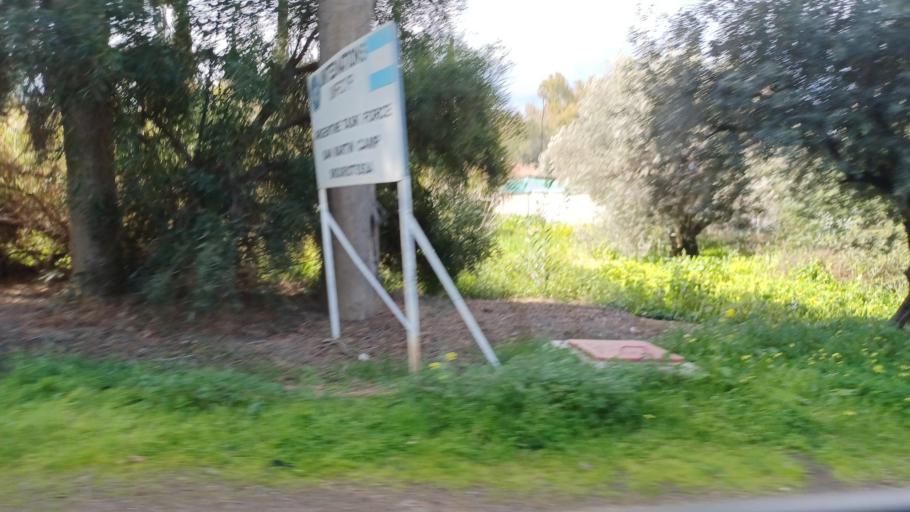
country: CY
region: Lefkosia
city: Lefka
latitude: 35.0921
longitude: 32.8856
